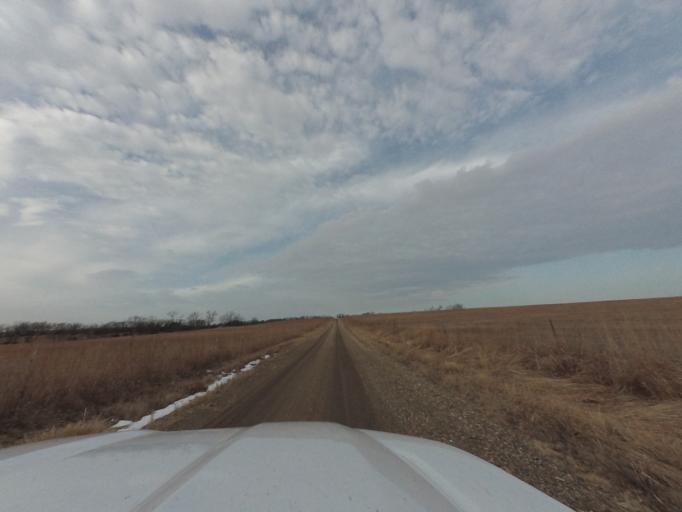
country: US
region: Kansas
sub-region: Chase County
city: Cottonwood Falls
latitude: 38.4785
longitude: -96.4144
